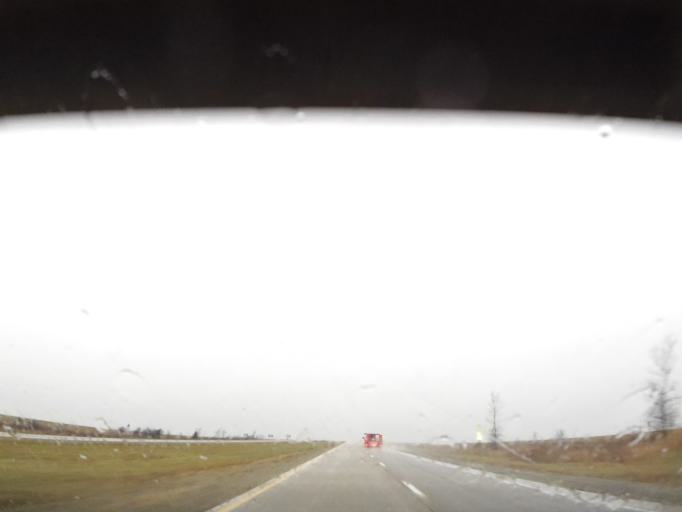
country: US
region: Iowa
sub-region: Cerro Gordo County
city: Mason City
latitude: 43.1055
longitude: -93.2606
